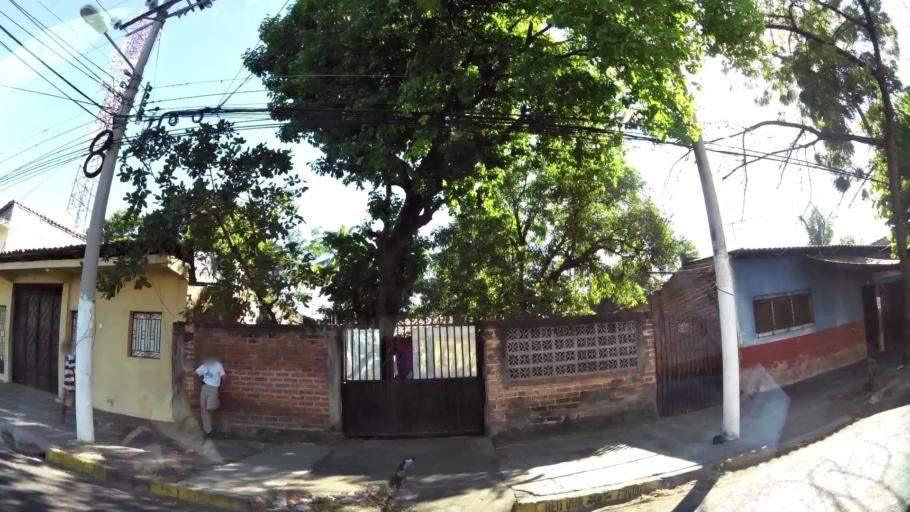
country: SV
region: San Miguel
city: San Miguel
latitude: 13.4738
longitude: -88.1796
